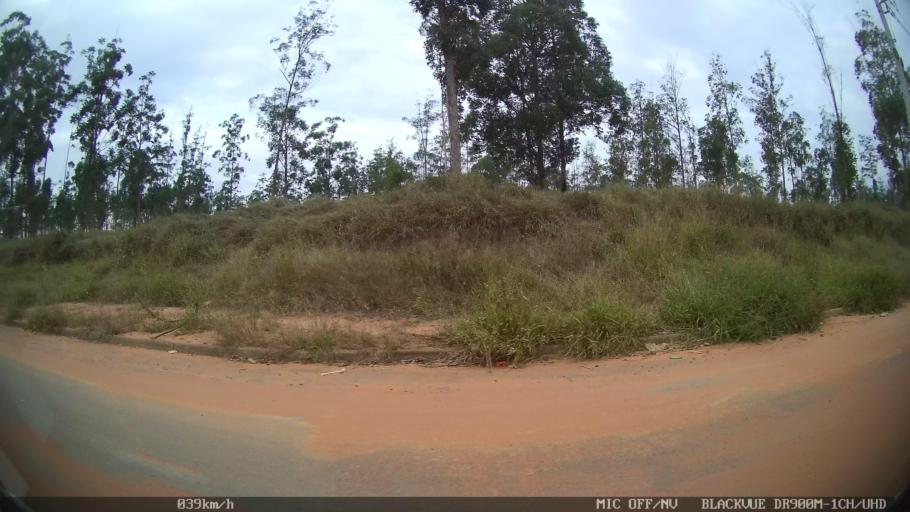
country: BR
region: Sao Paulo
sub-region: Americana
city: Americana
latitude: -22.6973
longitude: -47.3629
